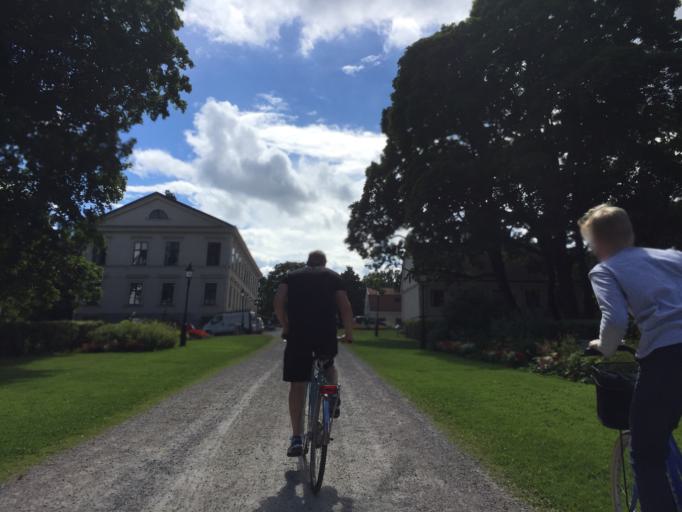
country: SE
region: OErebro
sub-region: Orebro Kommun
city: Orebro
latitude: 59.2705
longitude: 15.1488
